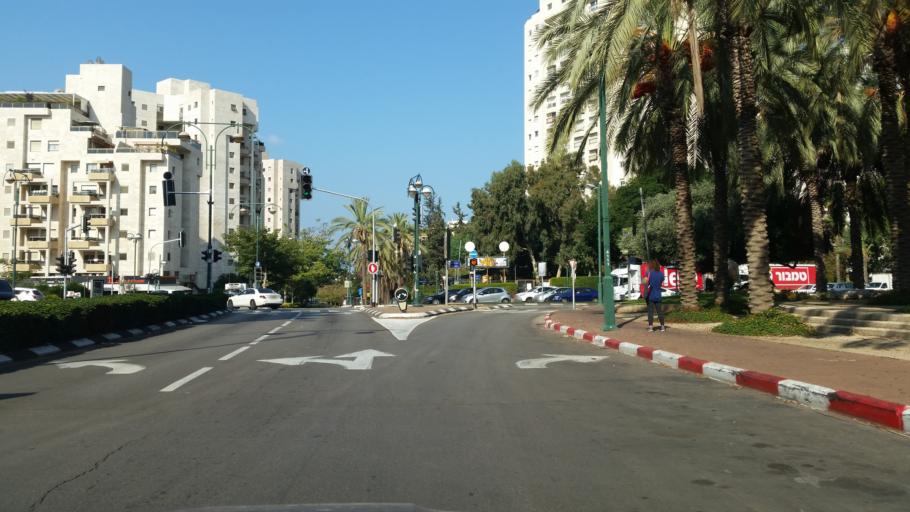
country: IL
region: Tel Aviv
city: Ramat HaSharon
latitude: 32.1515
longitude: 34.8425
